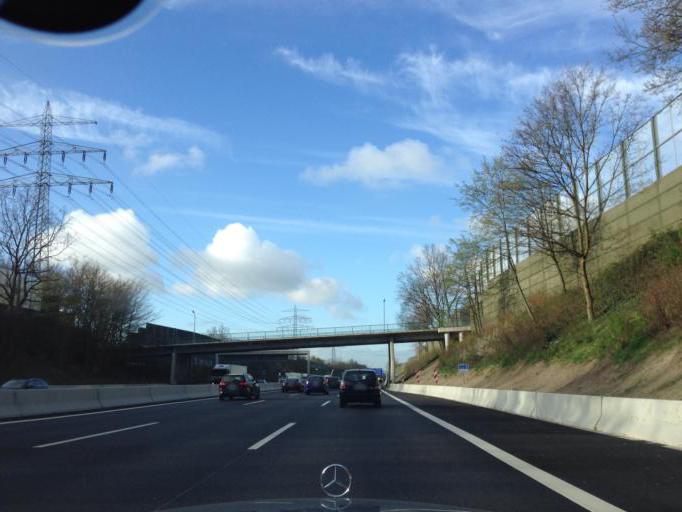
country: DE
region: Schleswig-Holstein
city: Oststeinbek
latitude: 53.5371
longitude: 10.1424
